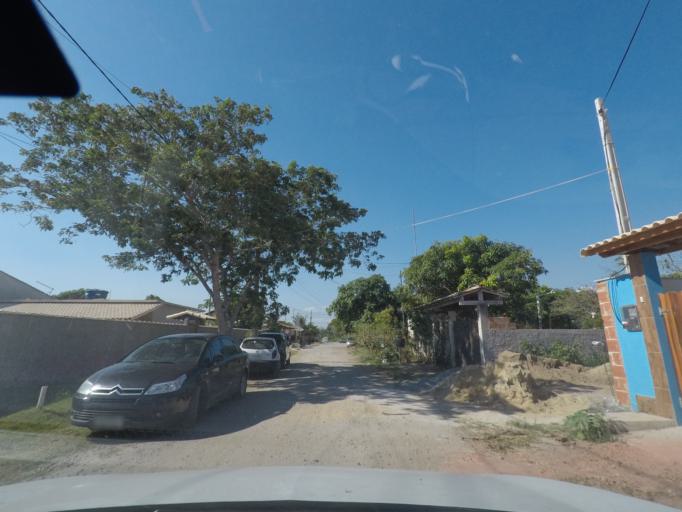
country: BR
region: Rio de Janeiro
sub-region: Marica
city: Marica
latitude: -22.9654
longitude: -42.9235
